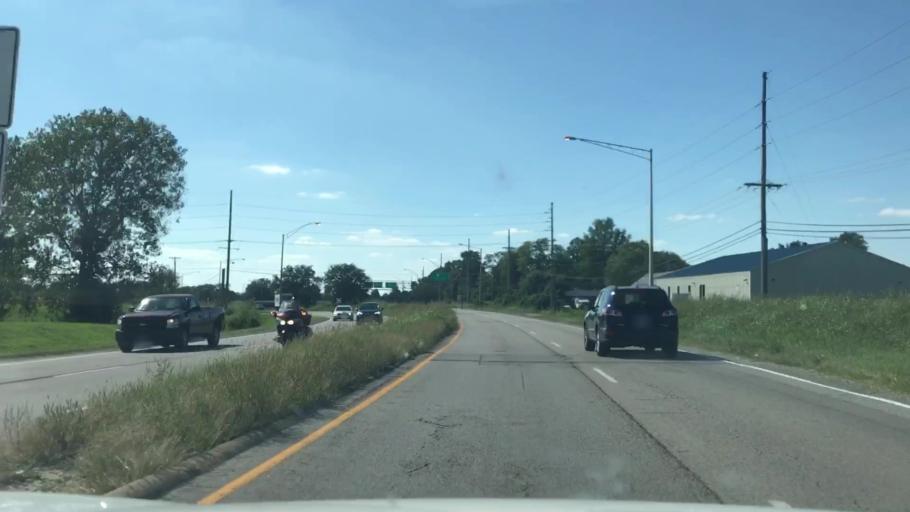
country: US
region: Illinois
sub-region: Saint Clair County
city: Swansea
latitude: 38.5475
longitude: -90.0558
